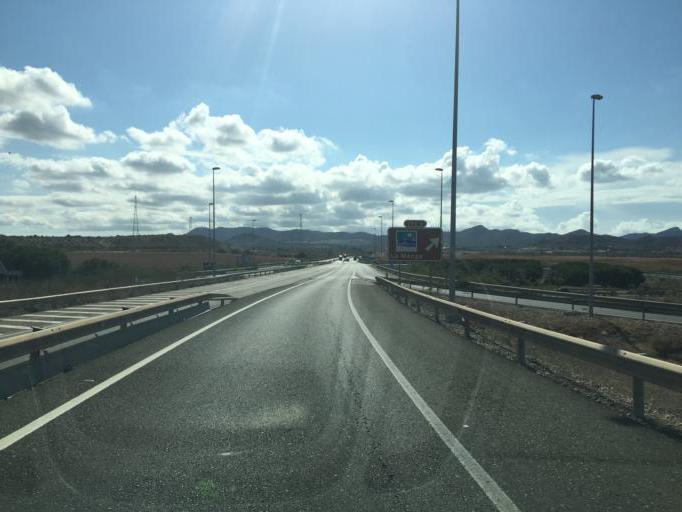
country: ES
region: Murcia
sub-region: Murcia
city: Cartagena
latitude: 37.6268
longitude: -0.9450
